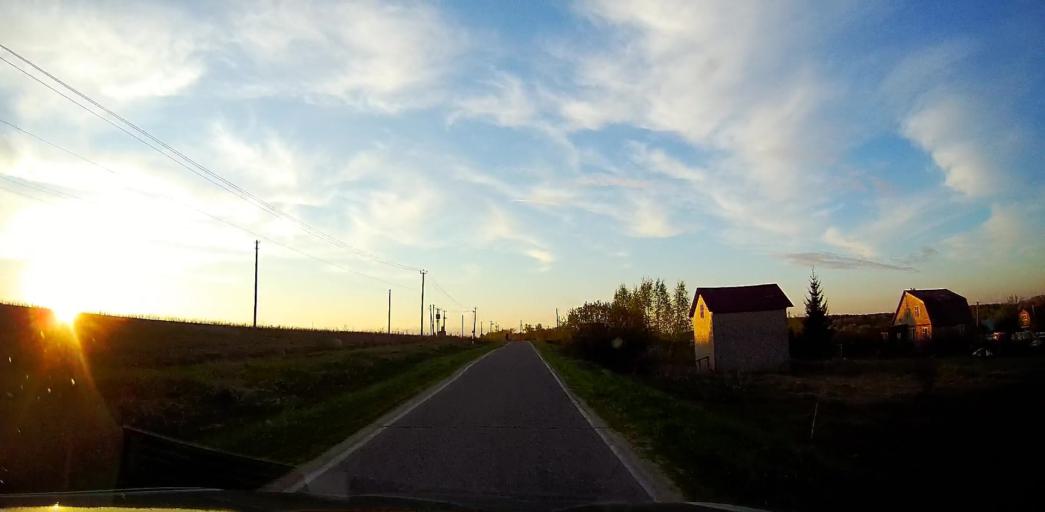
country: RU
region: Moskovskaya
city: Peski
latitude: 55.2262
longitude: 38.7350
